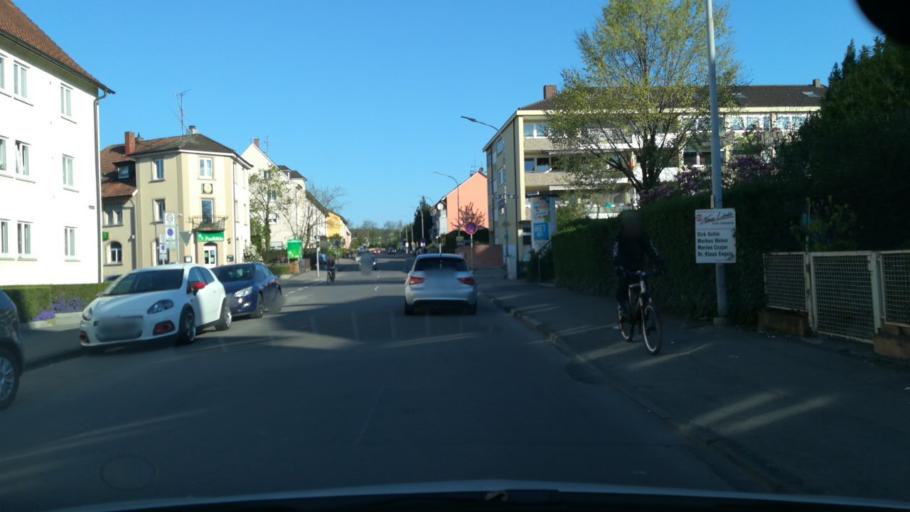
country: DE
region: Baden-Wuerttemberg
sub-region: Freiburg Region
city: Singen
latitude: 47.7647
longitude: 8.8439
